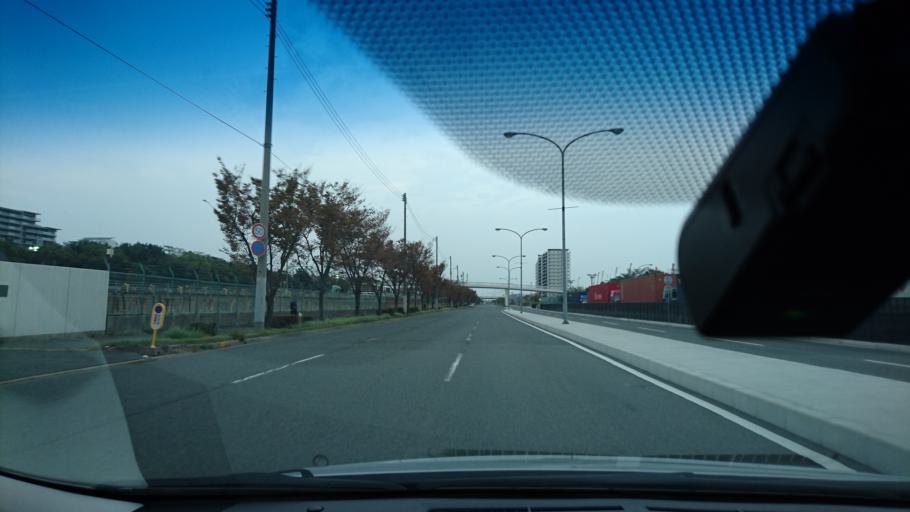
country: JP
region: Hyogo
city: Ashiya
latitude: 34.6824
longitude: 135.2633
